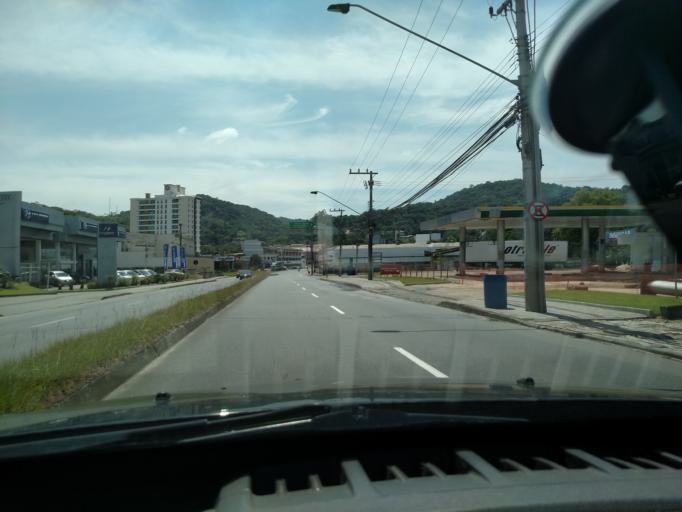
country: BR
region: Santa Catarina
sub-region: Blumenau
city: Blumenau
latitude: -26.8938
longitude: -49.0652
